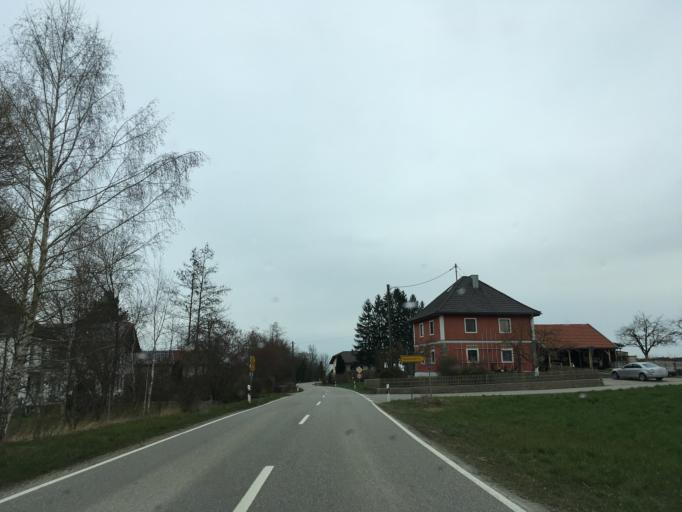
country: DE
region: Bavaria
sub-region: Upper Bavaria
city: Schnaitsee
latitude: 48.1039
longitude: 12.4097
